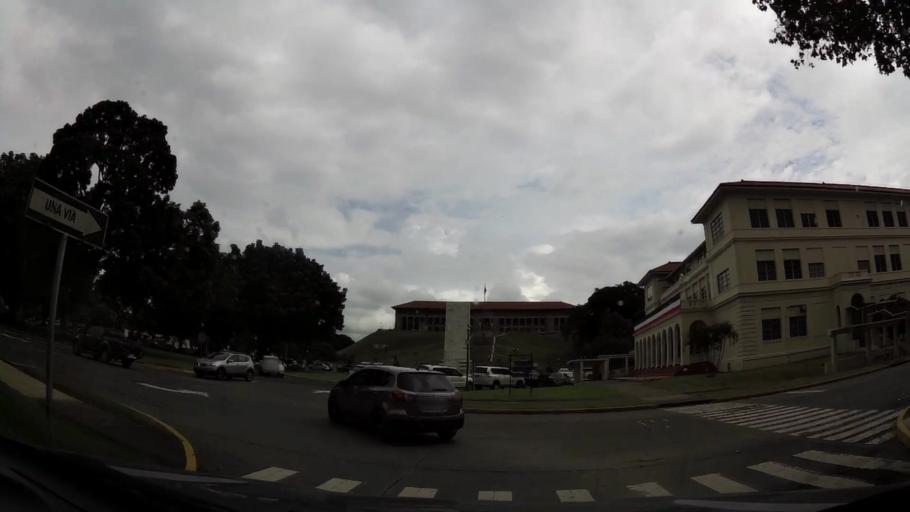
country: PA
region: Panama
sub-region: Distrito de Panama
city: Ancon
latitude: 8.9577
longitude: -79.5562
